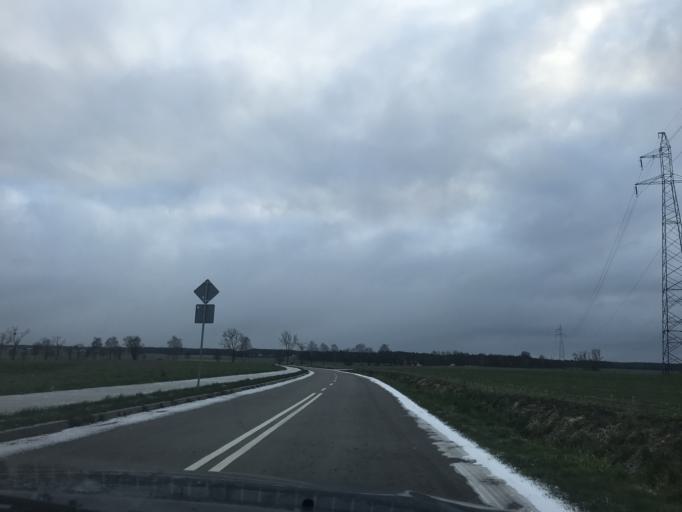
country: PL
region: Pomeranian Voivodeship
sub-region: Powiat chojnicki
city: Brusy
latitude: 53.8712
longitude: 17.7519
